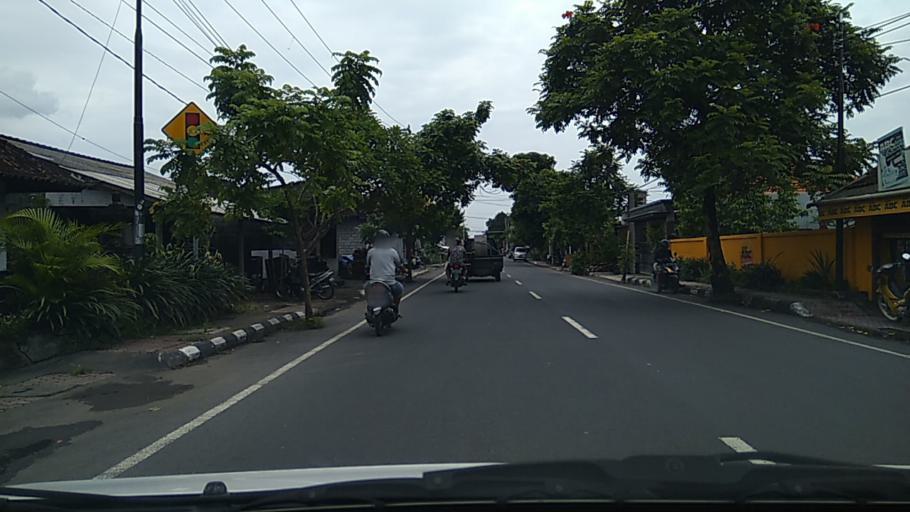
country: ID
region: Bali
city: Banjar Pesalakan
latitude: -8.5350
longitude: 115.3151
